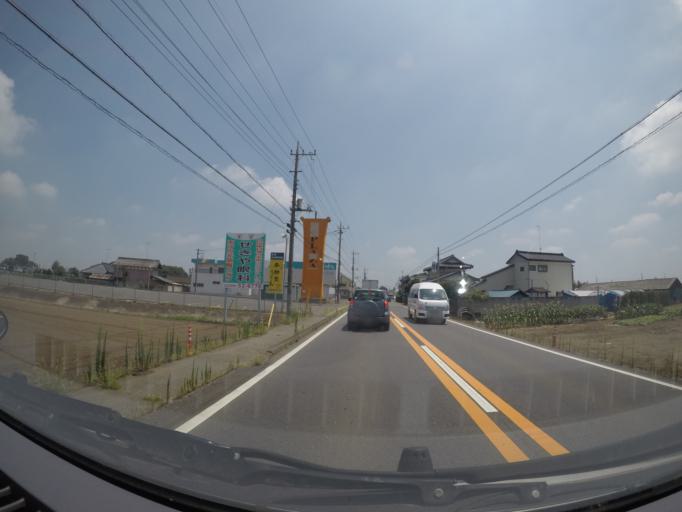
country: JP
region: Ibaraki
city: Yuki
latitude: 36.1918
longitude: 139.8808
